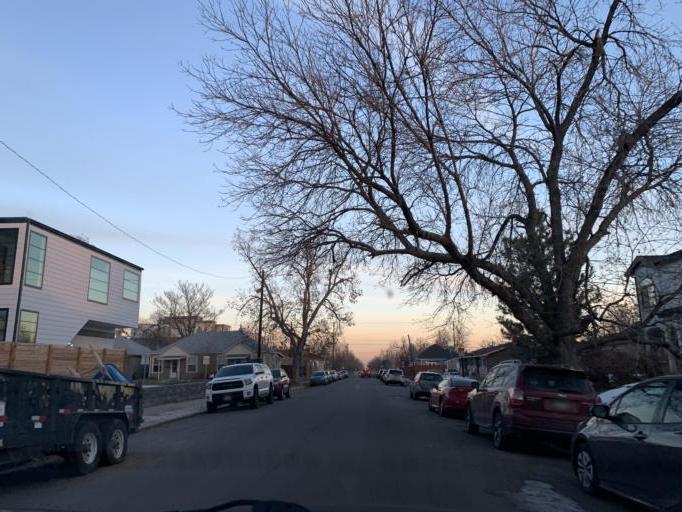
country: US
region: Colorado
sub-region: Adams County
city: Berkley
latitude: 39.7856
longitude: -105.0364
